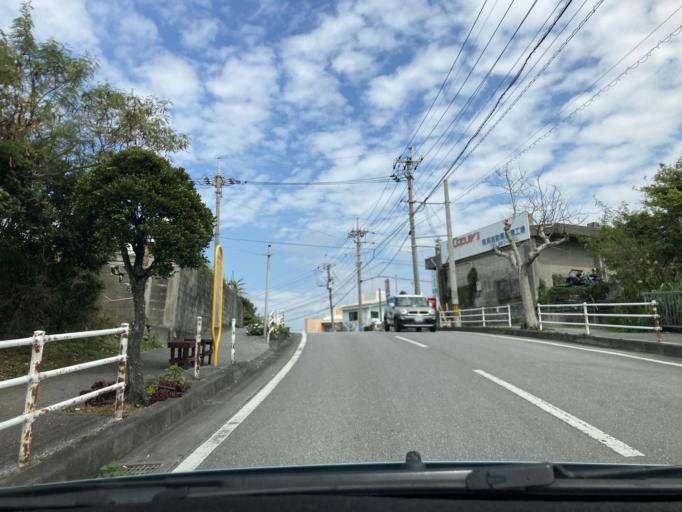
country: JP
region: Okinawa
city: Tomigusuku
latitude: 26.1862
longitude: 127.6960
